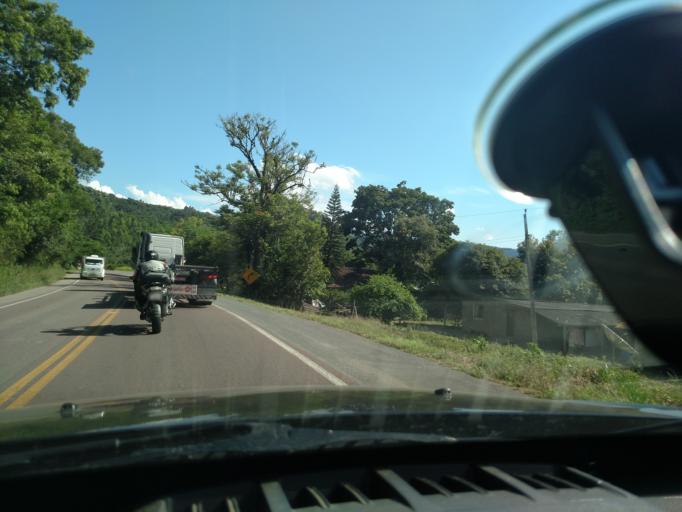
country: BR
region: Santa Catarina
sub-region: Ibirama
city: Ibirama
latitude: -27.0630
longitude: -49.4158
